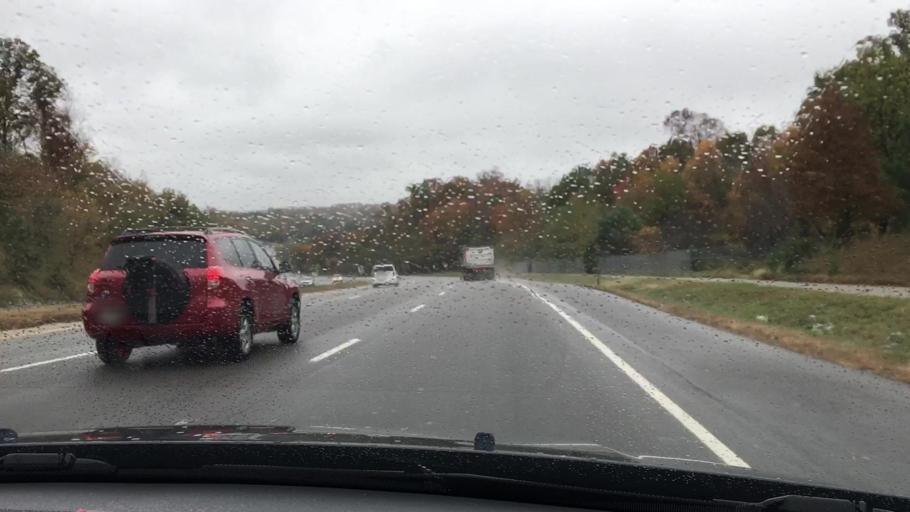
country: US
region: Virginia
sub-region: Prince William County
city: Woodbridge
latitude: 38.6895
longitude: -77.2572
